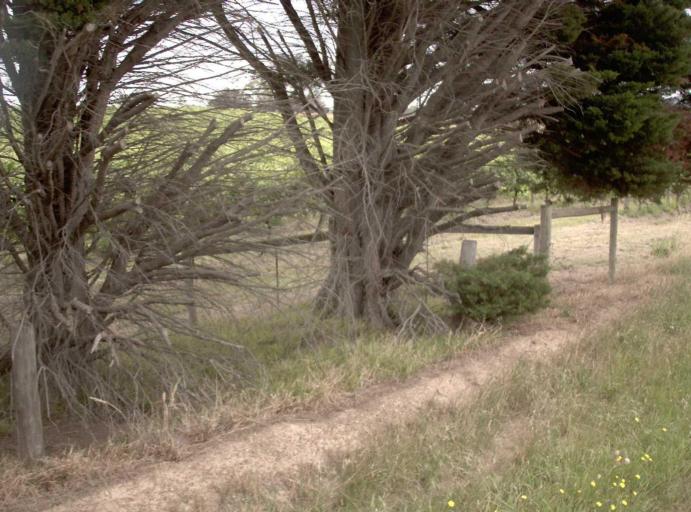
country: AU
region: Victoria
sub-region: Yarra Ranges
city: Yarra Glen
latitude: -37.6580
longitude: 145.3972
